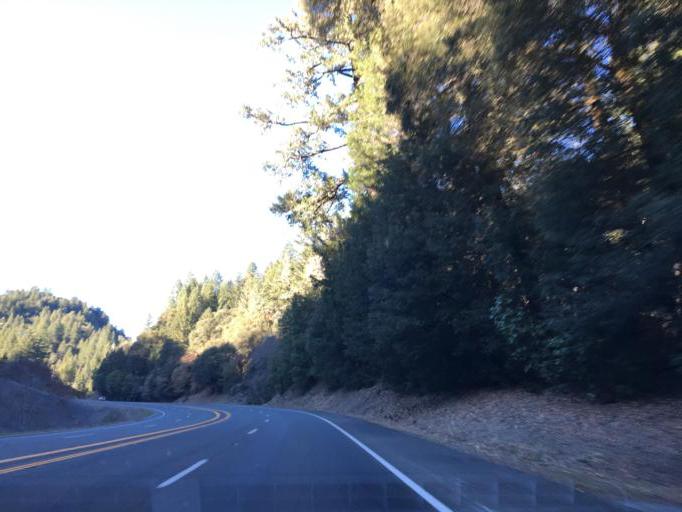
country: US
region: California
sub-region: Mendocino County
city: Laytonville
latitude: 39.5781
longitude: -123.4405
